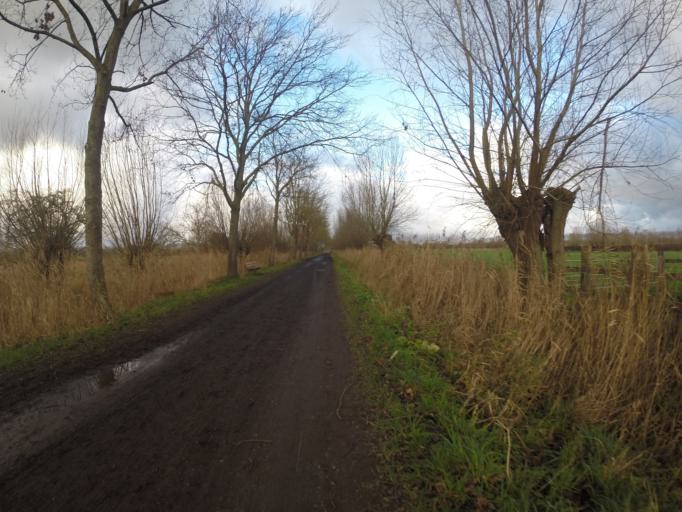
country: BE
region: Flanders
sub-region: Provincie West-Vlaanderen
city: Sint-Kruis
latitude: 51.1806
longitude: 3.2734
